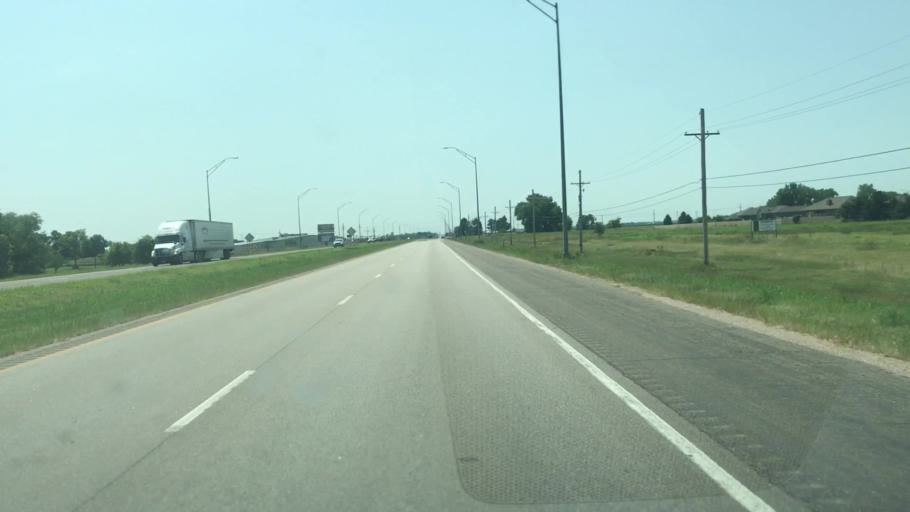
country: US
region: Nebraska
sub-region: Hall County
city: Grand Island
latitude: 40.8779
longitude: -98.3783
